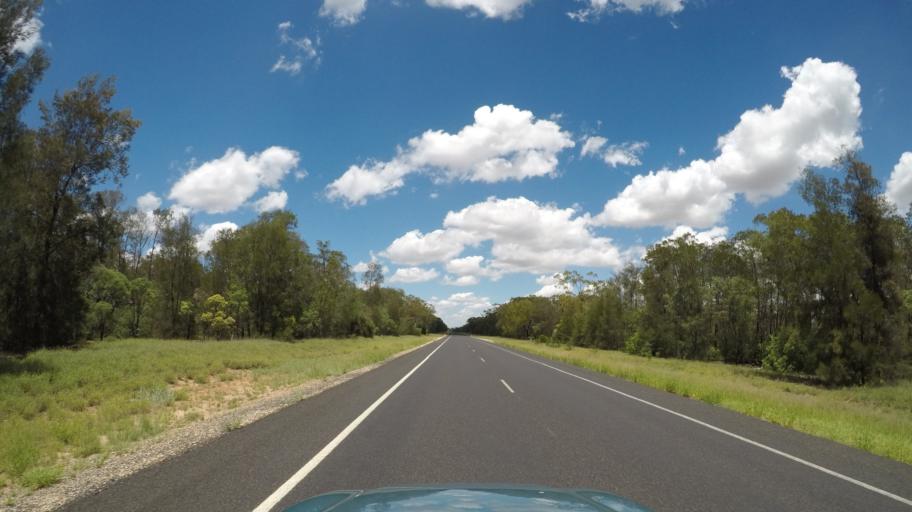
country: AU
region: Queensland
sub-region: Goondiwindi
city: Goondiwindi
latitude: -28.0584
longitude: 150.7691
